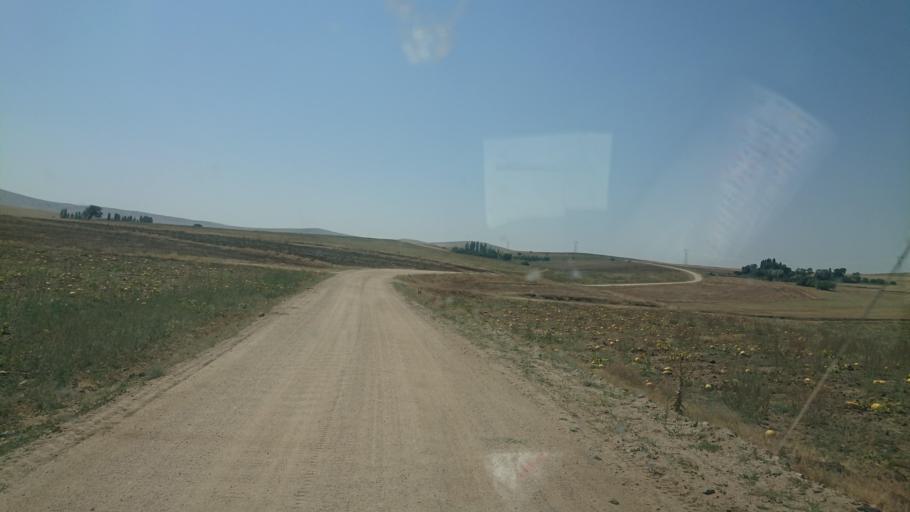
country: TR
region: Aksaray
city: Agacoren
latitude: 38.8118
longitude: 33.9529
